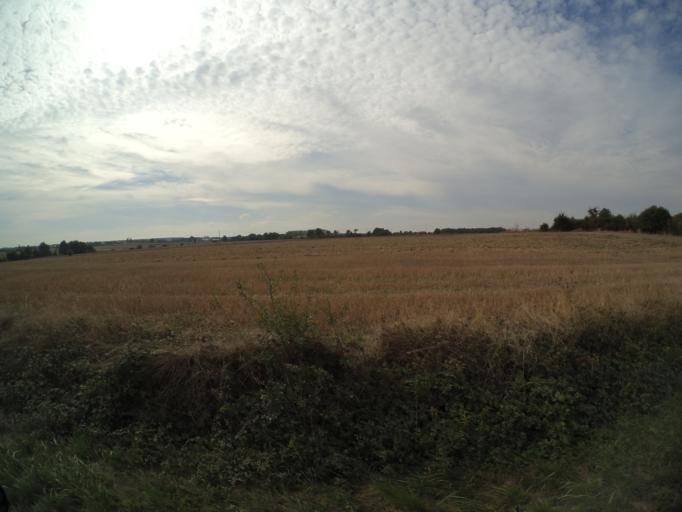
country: FR
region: Pays de la Loire
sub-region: Departement de Maine-et-Loire
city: Martigne-Briand
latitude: 47.2092
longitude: -0.4833
